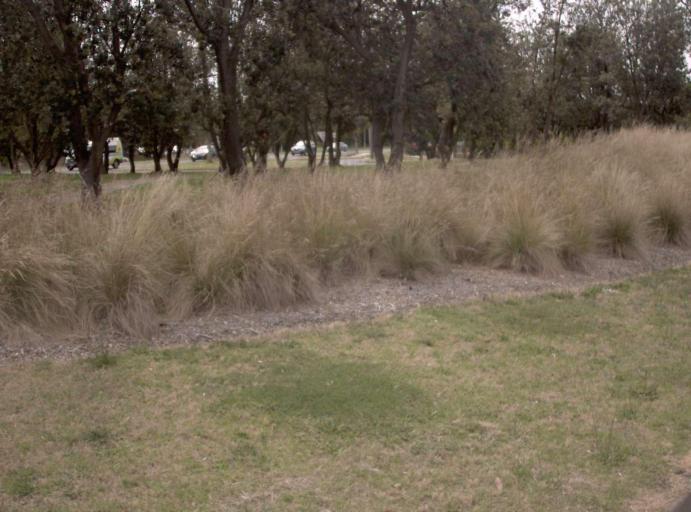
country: AU
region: Victoria
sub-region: Frankston
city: Frankston South
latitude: -38.1533
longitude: 145.1335
